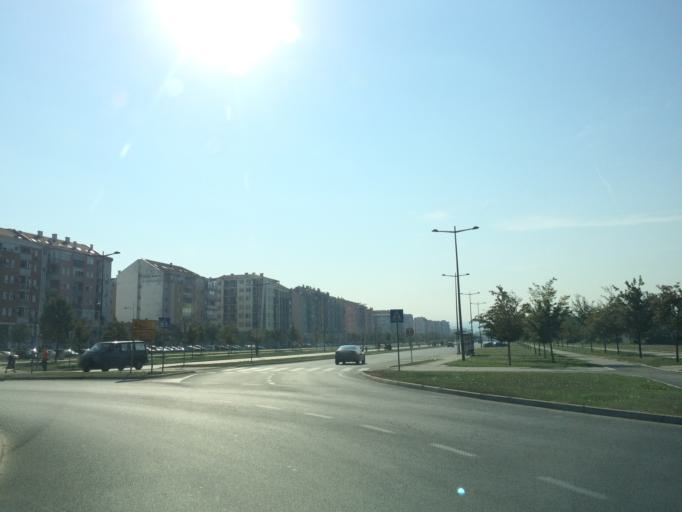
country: RS
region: Autonomna Pokrajina Vojvodina
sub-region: Juznobacki Okrug
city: Novi Sad
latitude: 45.2601
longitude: 19.8084
